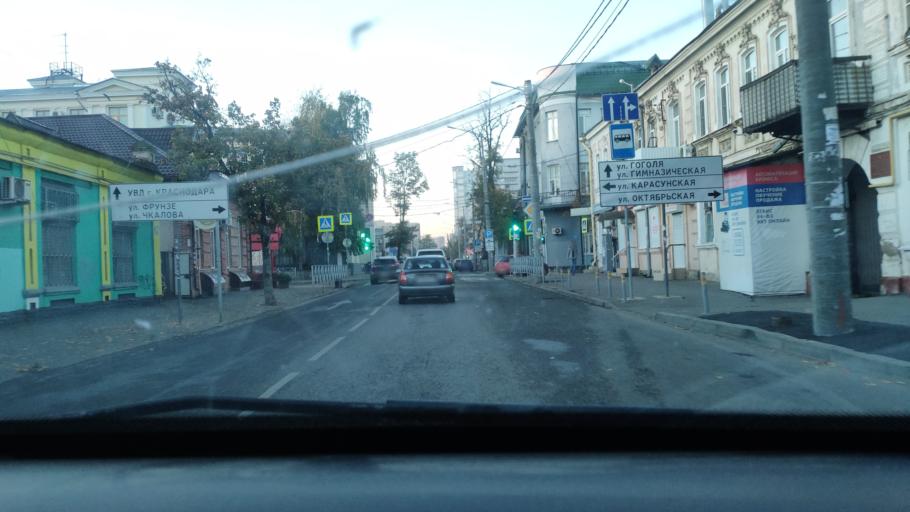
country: RU
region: Krasnodarskiy
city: Krasnodar
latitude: 45.0292
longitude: 38.9698
